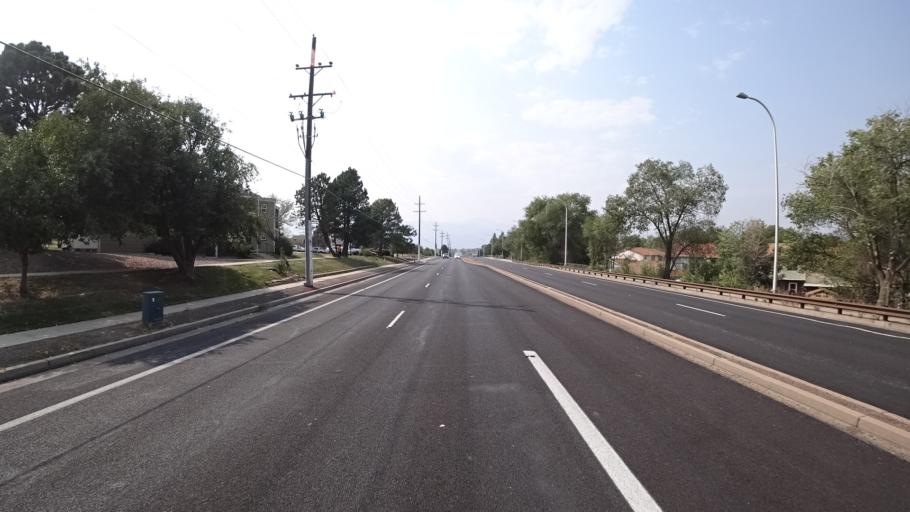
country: US
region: Colorado
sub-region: El Paso County
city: Stratmoor
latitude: 38.8253
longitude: -104.7496
